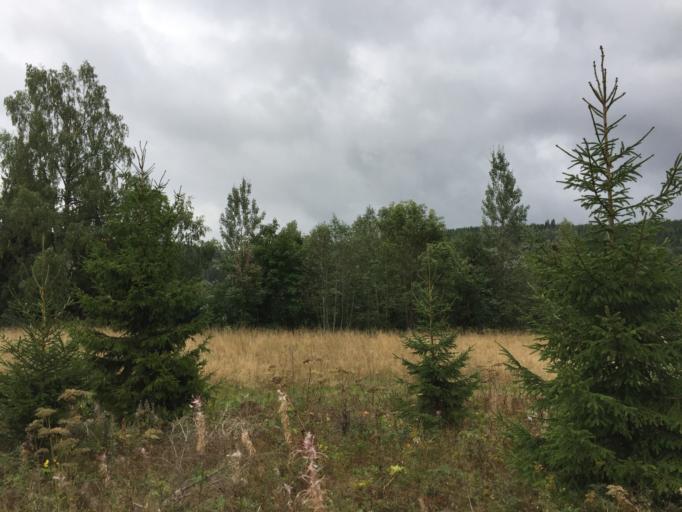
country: NO
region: Akershus
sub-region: Baerum
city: Sandvika
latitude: 60.0190
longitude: 10.5571
